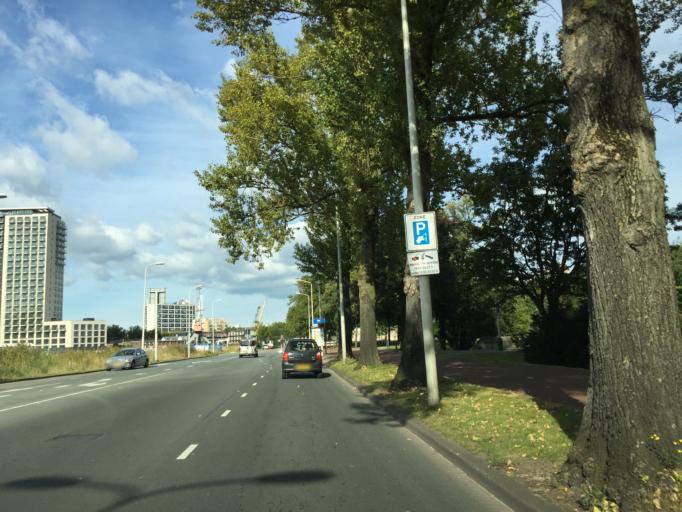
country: NL
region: South Holland
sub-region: Gemeente Den Haag
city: The Hague
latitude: 52.0566
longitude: 4.3118
